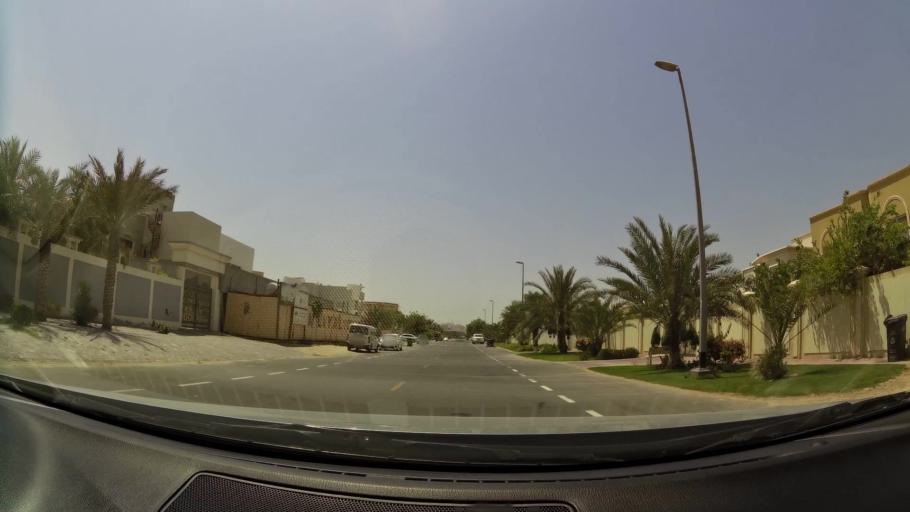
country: AE
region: Dubai
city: Dubai
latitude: 25.0989
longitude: 55.2182
